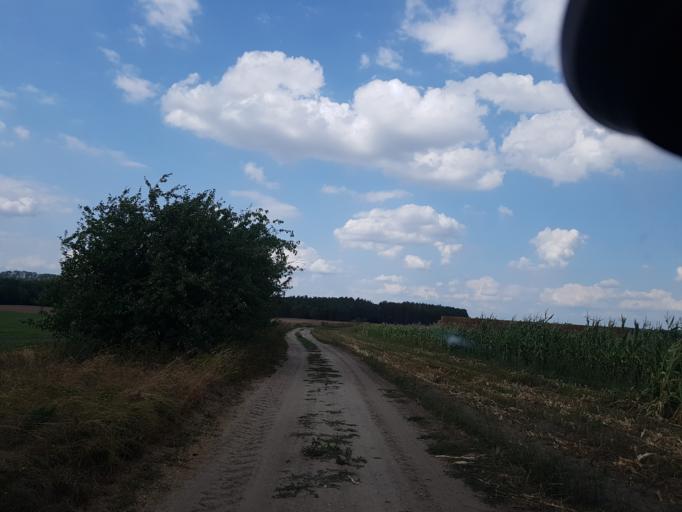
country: DE
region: Brandenburg
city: Calau
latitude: 51.7572
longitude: 13.9514
